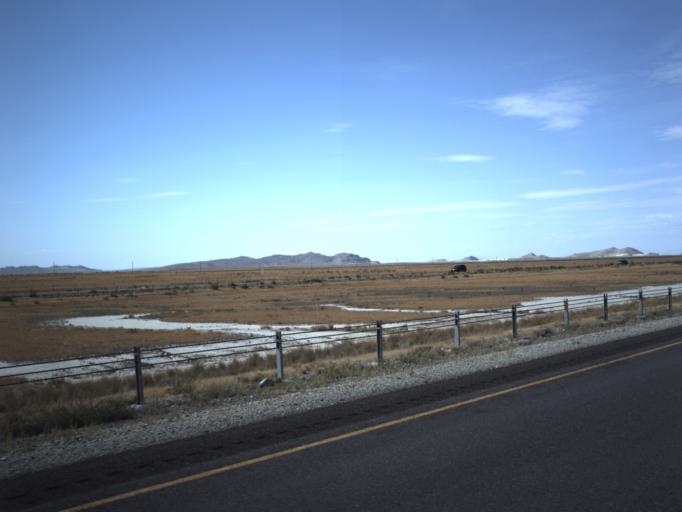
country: US
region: Utah
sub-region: Tooele County
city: Grantsville
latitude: 40.7267
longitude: -113.2053
